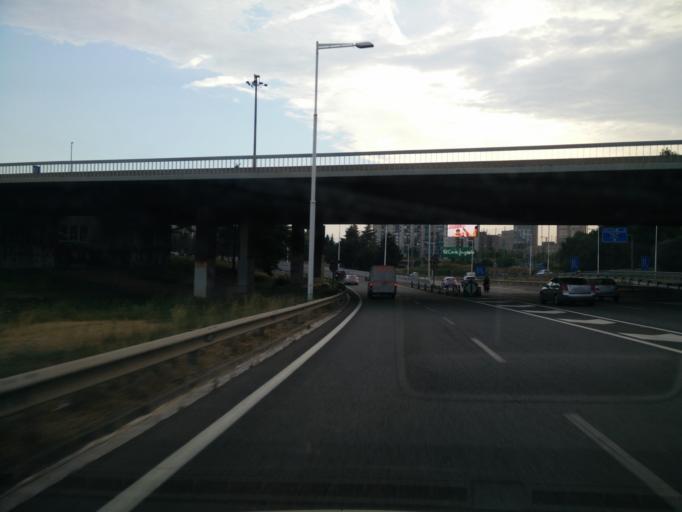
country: ES
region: Catalonia
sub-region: Provincia de Barcelona
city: Sant Adria de Besos
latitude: 41.4262
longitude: 2.2163
